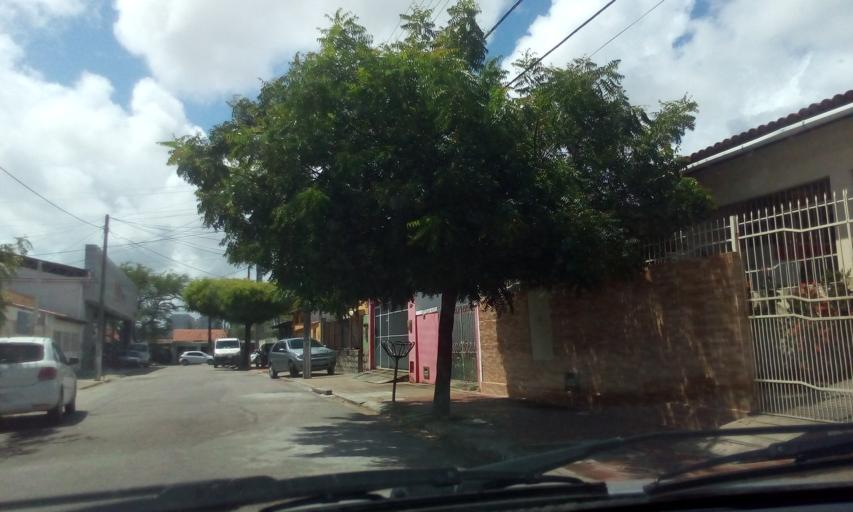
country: BR
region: Rio Grande do Norte
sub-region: Natal
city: Natal
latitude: -5.8653
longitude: -35.2054
